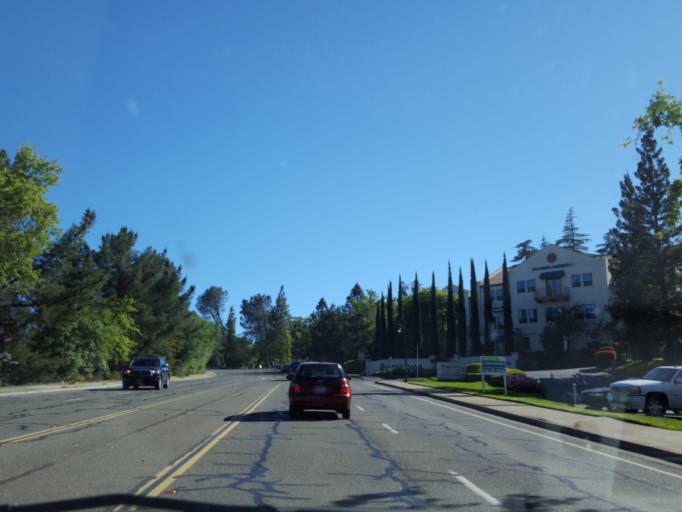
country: US
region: California
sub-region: Placer County
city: Auburn
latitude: 38.8899
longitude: -121.0768
